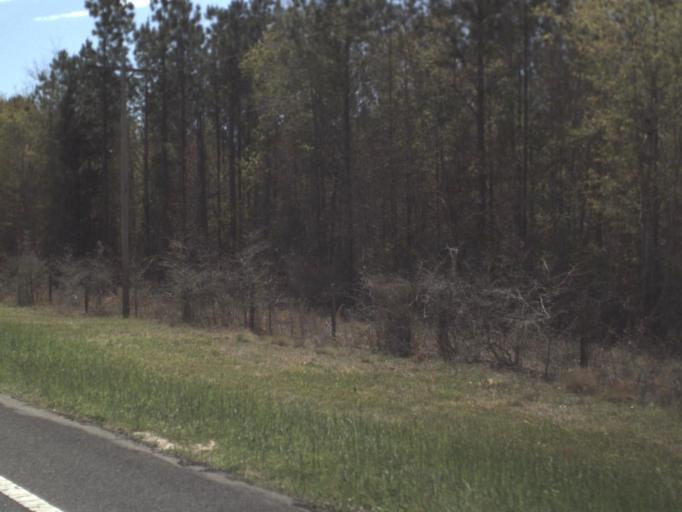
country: US
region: Florida
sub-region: Walton County
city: DeFuniak Springs
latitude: 30.7575
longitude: -85.9590
